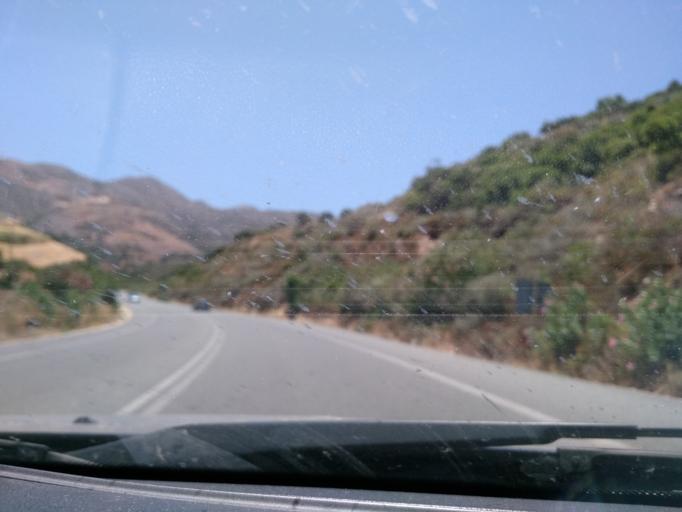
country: GR
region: Crete
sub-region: Nomos Rethymnis
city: Anogeia
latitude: 35.3915
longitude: 24.9208
